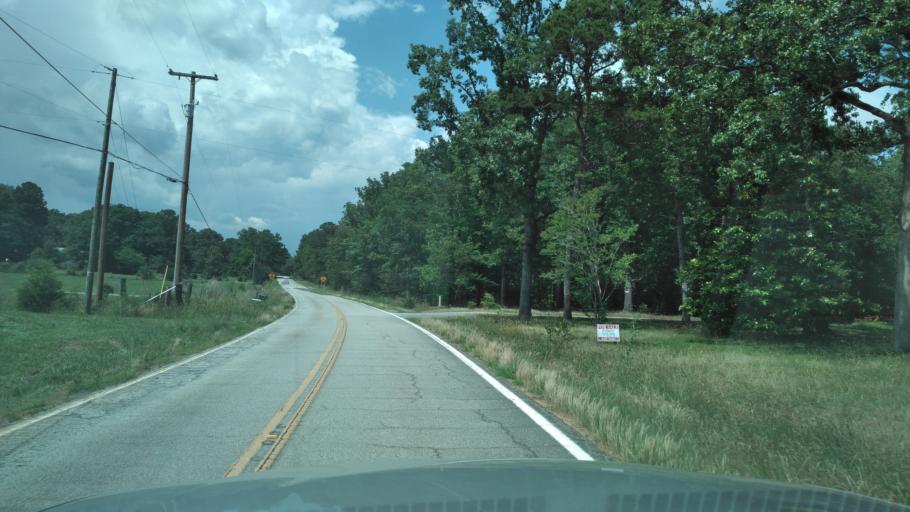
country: US
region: South Carolina
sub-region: Laurens County
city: Laurens
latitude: 34.5110
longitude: -82.0943
